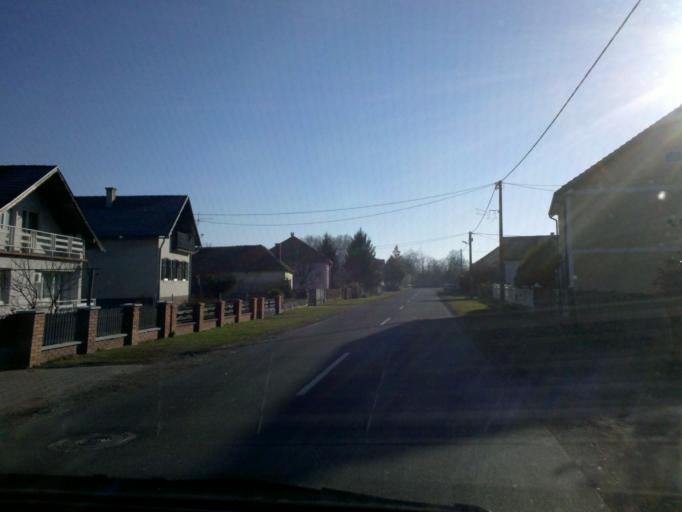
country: HR
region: Medimurska
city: Hodosan
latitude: 46.3994
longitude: 16.6359
